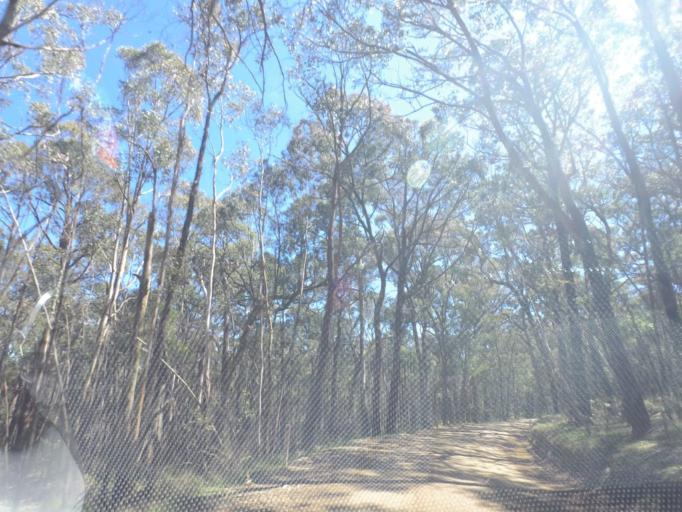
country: AU
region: Victoria
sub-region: Hume
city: Sunbury
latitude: -37.3928
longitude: 144.5675
